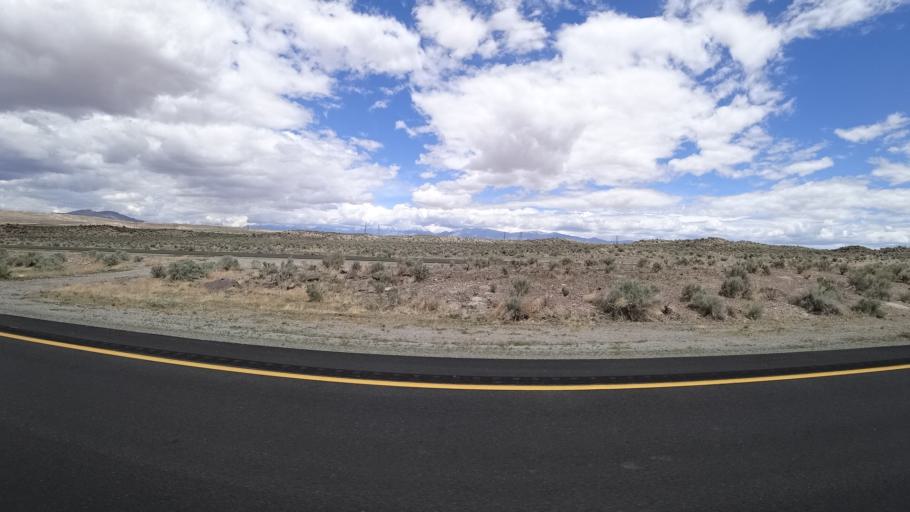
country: US
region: California
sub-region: Inyo County
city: West Bishop
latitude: 37.4283
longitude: -118.5616
